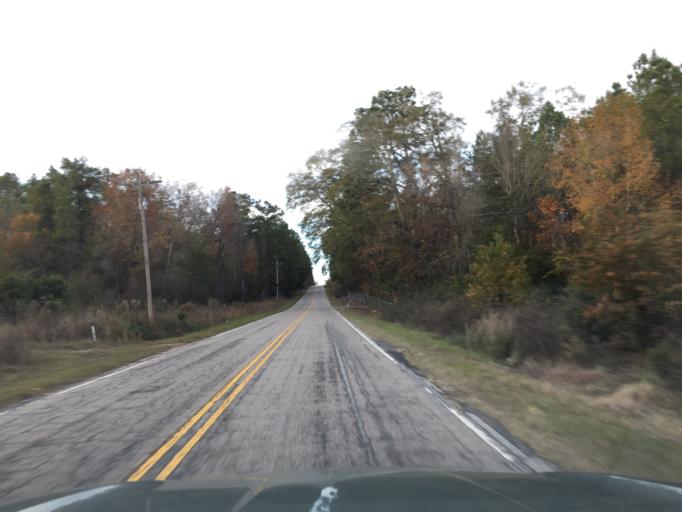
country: US
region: South Carolina
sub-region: Lexington County
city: Red Bank
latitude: 33.7425
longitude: -81.3631
